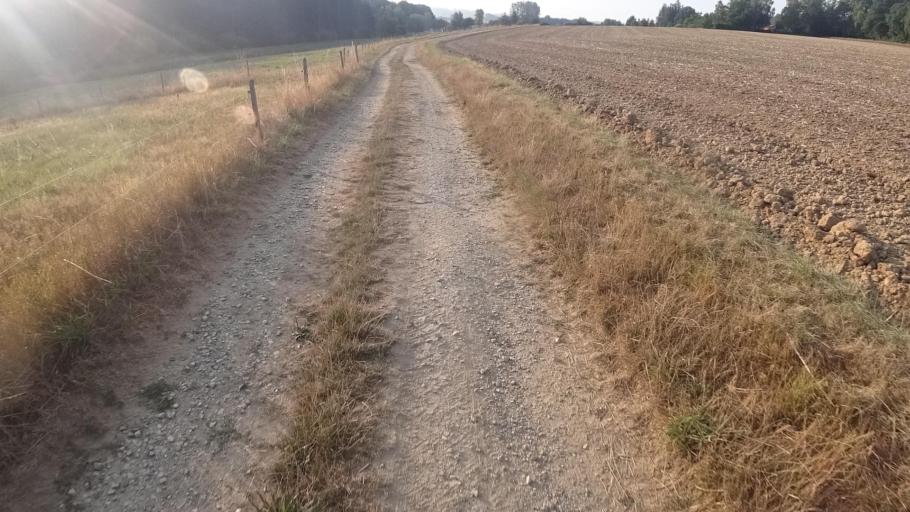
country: DE
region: Rheinland-Pfalz
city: Holzbach
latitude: 49.9592
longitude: 7.5179
